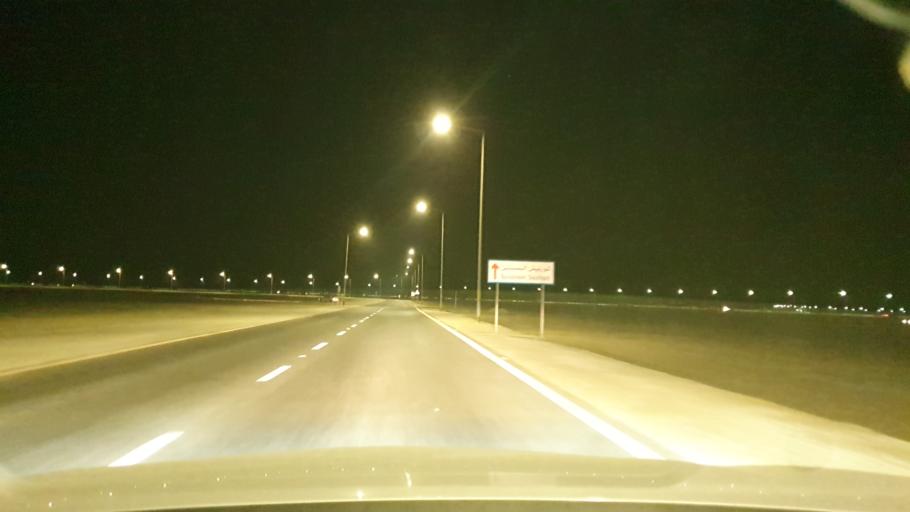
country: BH
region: Muharraq
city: Al Muharraq
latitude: 26.2844
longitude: 50.5821
